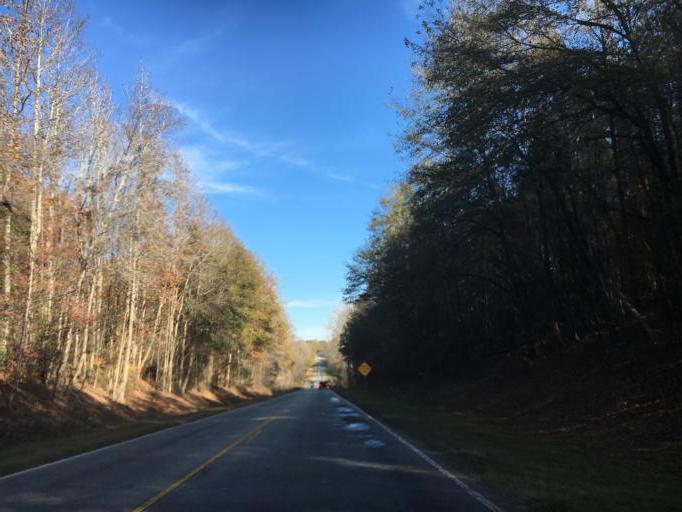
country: US
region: South Carolina
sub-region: Spartanburg County
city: Wellford
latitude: 34.9670
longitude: -82.1060
